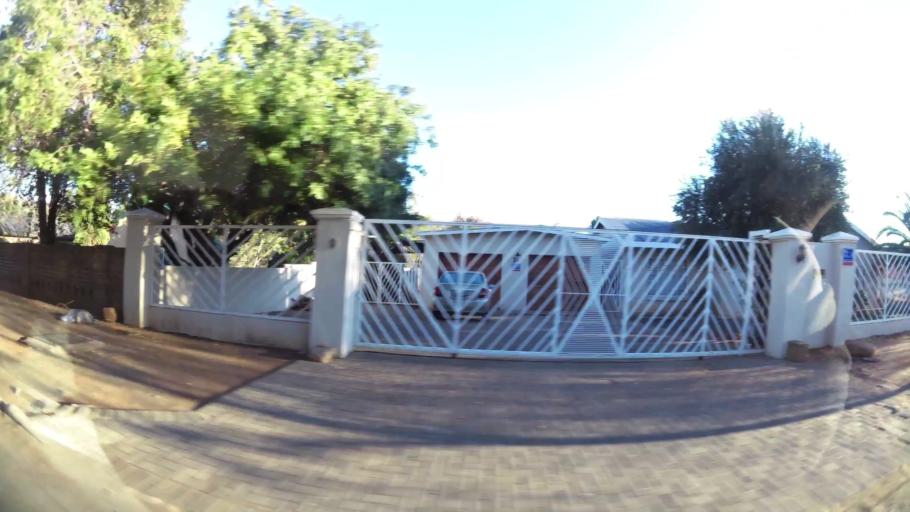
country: ZA
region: Northern Cape
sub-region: Frances Baard District Municipality
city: Kimberley
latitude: -28.7543
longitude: 24.7379
